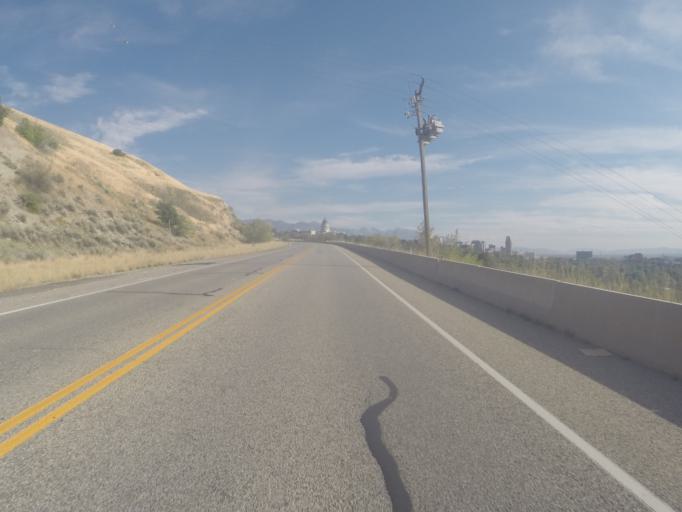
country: US
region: Utah
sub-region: Salt Lake County
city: Salt Lake City
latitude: 40.7871
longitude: -111.8965
